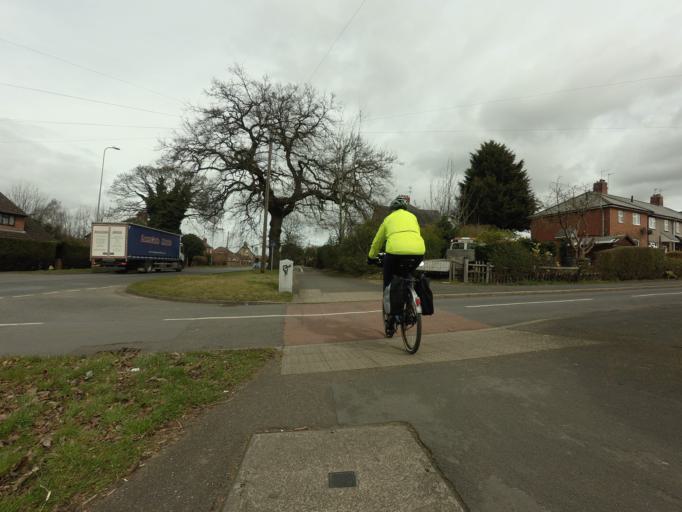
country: GB
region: England
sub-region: Lincolnshire
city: Grantham
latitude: 52.9211
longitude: -0.6332
